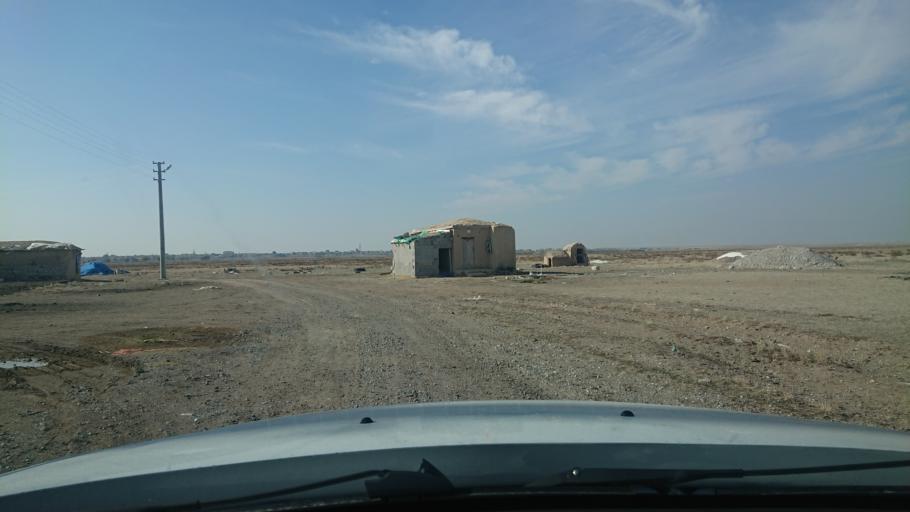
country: TR
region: Aksaray
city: Sultanhani
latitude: 38.2609
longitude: 33.4726
